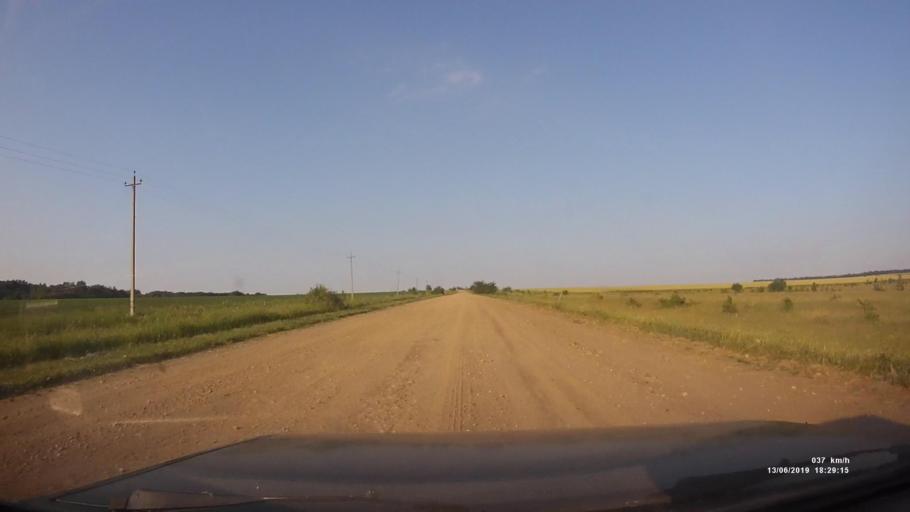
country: RU
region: Rostov
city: Kazanskaya
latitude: 49.8588
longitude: 41.3391
